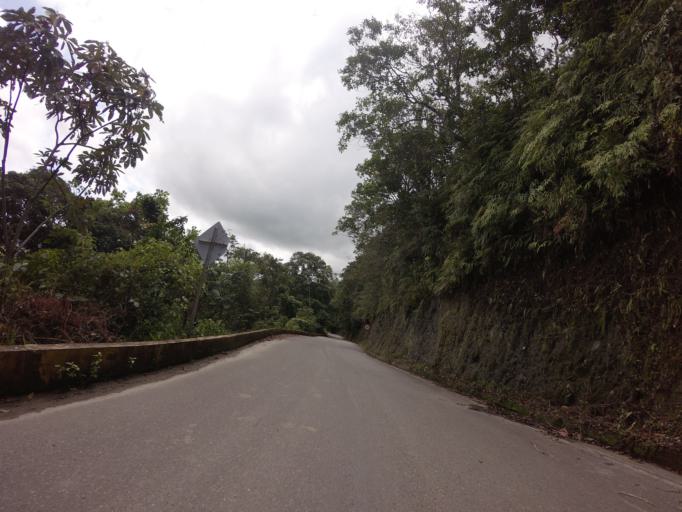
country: CO
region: Caldas
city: Victoria
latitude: 5.3257
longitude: -74.9244
